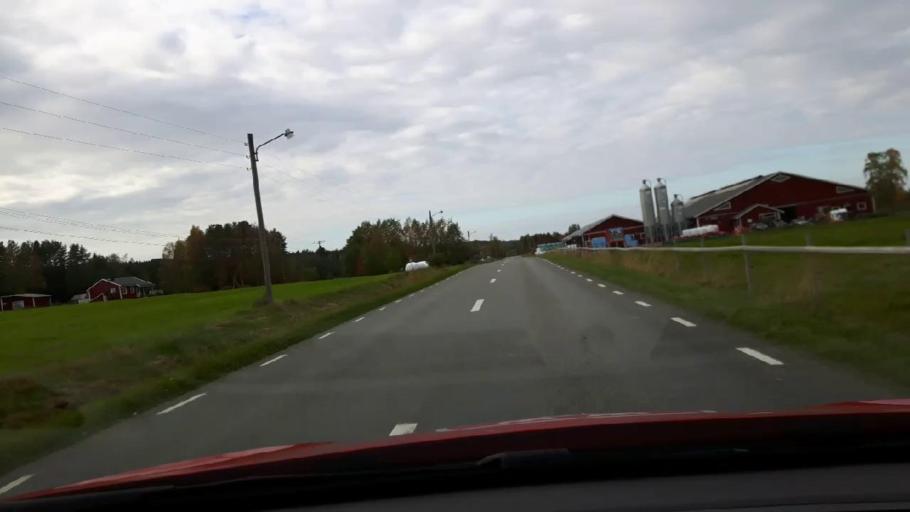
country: SE
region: Jaemtland
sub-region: Krokoms Kommun
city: Krokom
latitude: 63.1644
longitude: 14.1204
